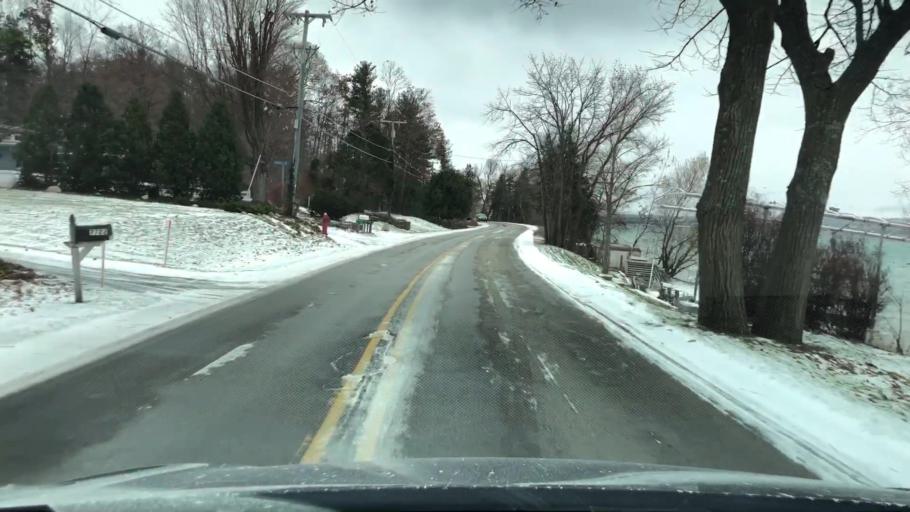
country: US
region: Michigan
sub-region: Grand Traverse County
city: Traverse City
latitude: 44.7997
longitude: -85.5835
